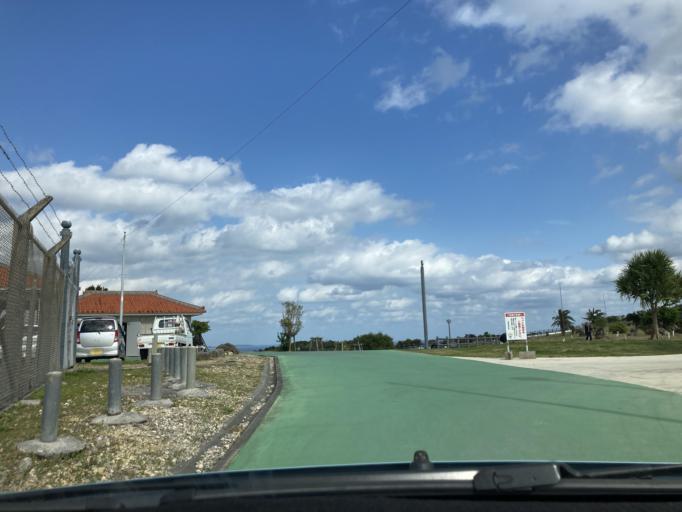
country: JP
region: Okinawa
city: Ginowan
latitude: 26.1858
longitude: 127.7623
